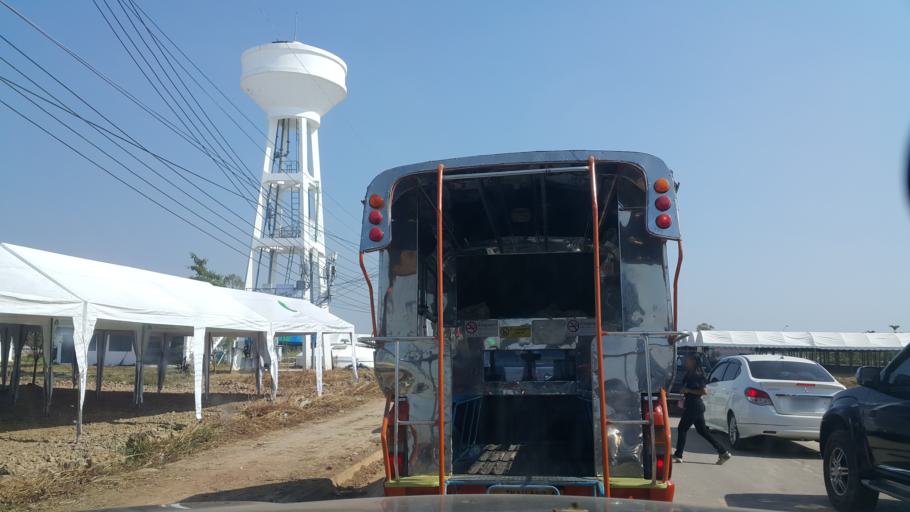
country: TH
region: Khon Kaen
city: Khon Kaen
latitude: 16.5131
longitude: 102.8704
